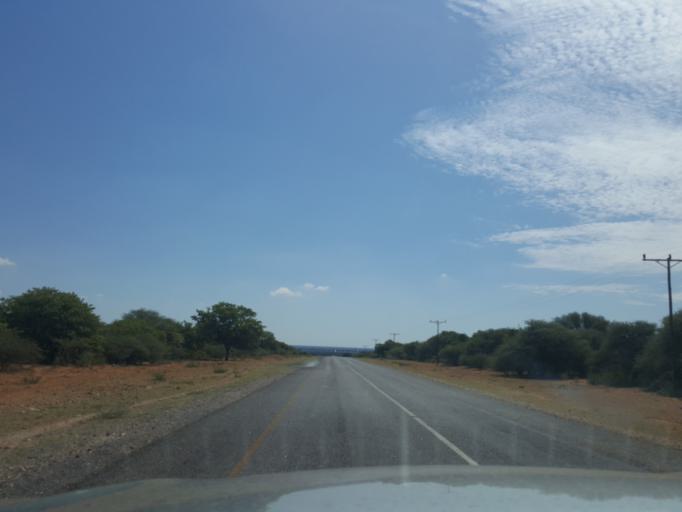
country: BW
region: Kweneng
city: Letlhakeng
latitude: -24.1224
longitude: 25.0882
